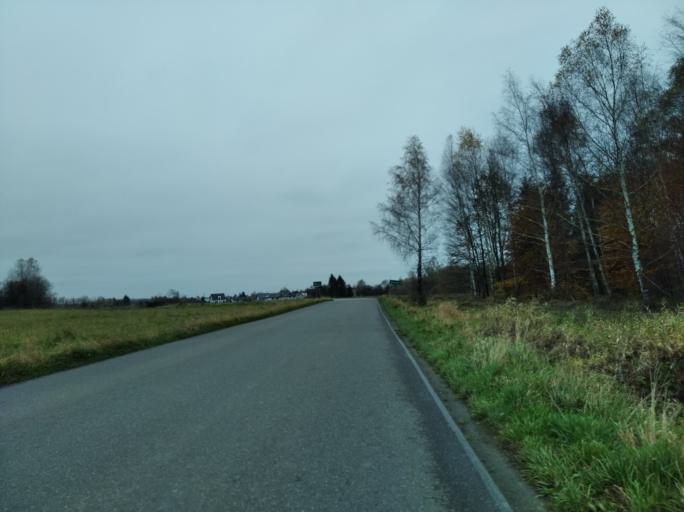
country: PL
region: Subcarpathian Voivodeship
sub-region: Powiat krosnienski
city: Chorkowka
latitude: 49.6775
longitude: 21.6797
